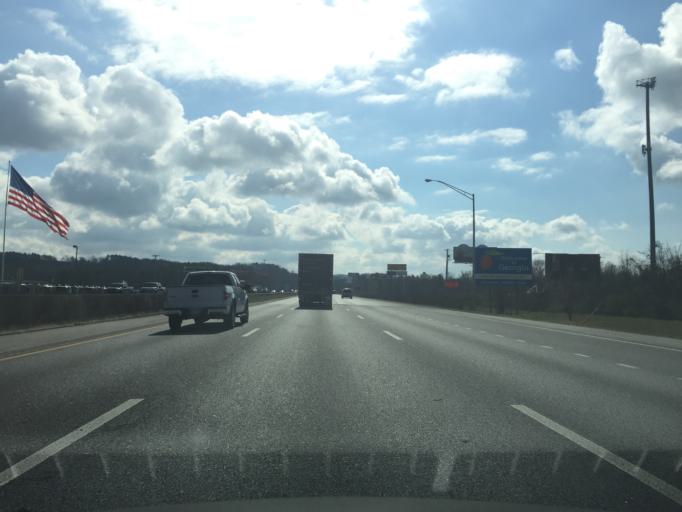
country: US
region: Georgia
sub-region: Catoosa County
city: Indian Springs
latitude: 34.9864
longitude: -85.2019
